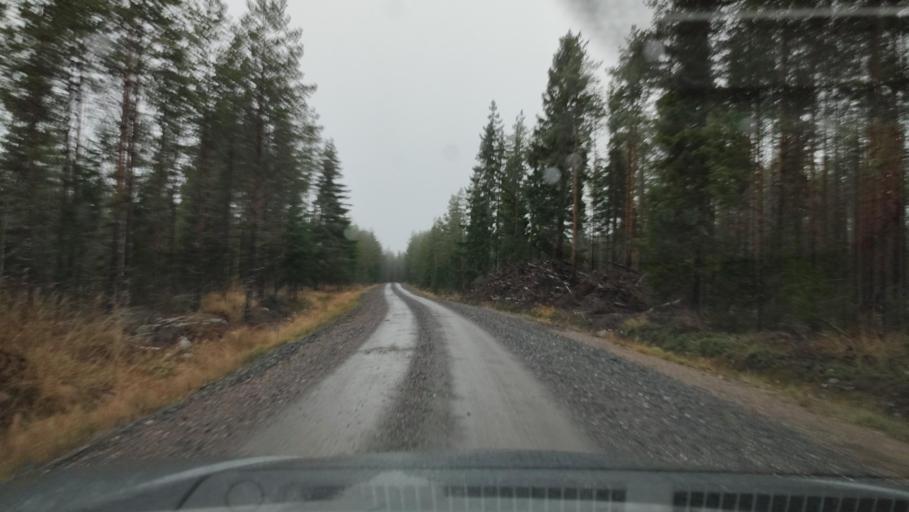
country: FI
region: Southern Ostrobothnia
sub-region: Suupohja
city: Karijoki
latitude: 62.1750
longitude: 21.7007
